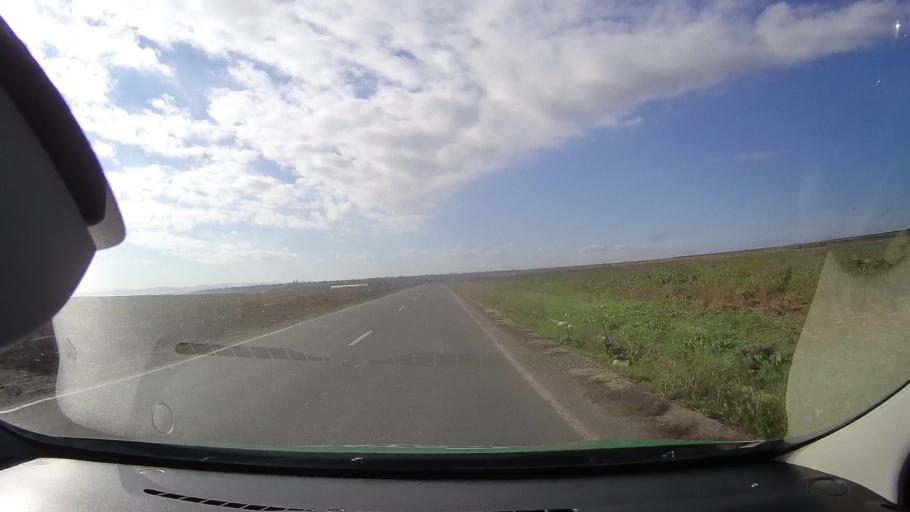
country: RO
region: Tulcea
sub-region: Comuna Sarichioi
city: Sarichioi
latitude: 44.9674
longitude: 28.8670
